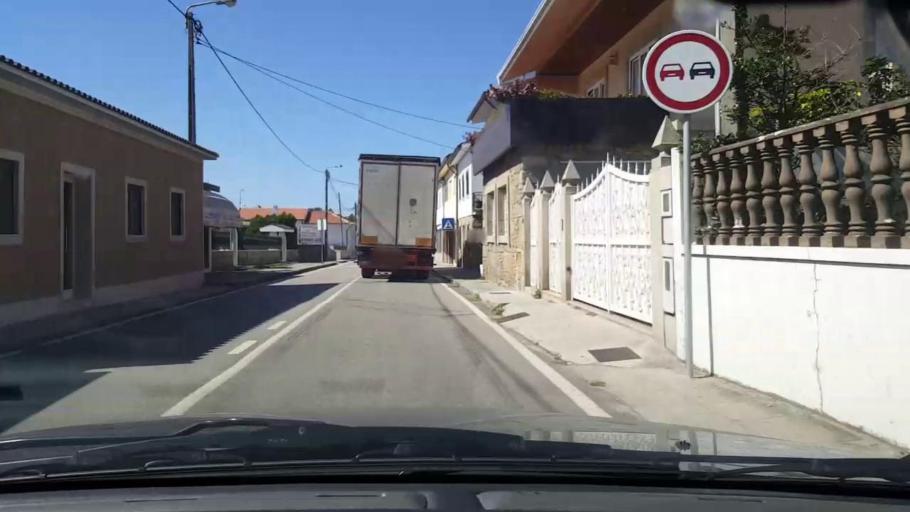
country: PT
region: Porto
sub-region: Vila do Conde
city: Arvore
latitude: 41.3381
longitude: -8.6850
